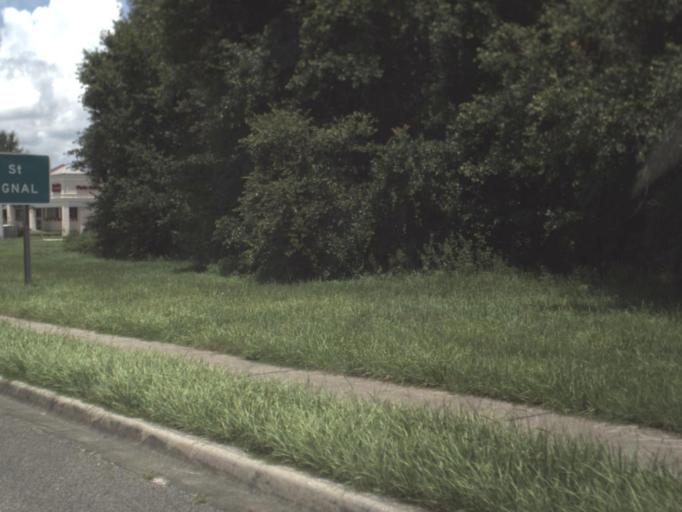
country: US
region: Florida
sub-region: Hernando County
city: South Brooksville
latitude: 28.5398
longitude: -82.4016
